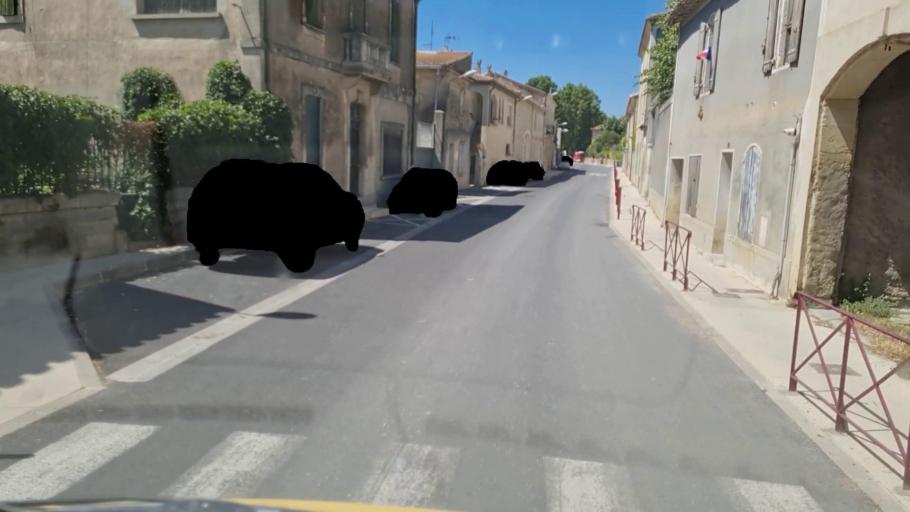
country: FR
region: Languedoc-Roussillon
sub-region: Departement du Gard
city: Le Cailar
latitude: 43.6758
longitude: 4.2371
